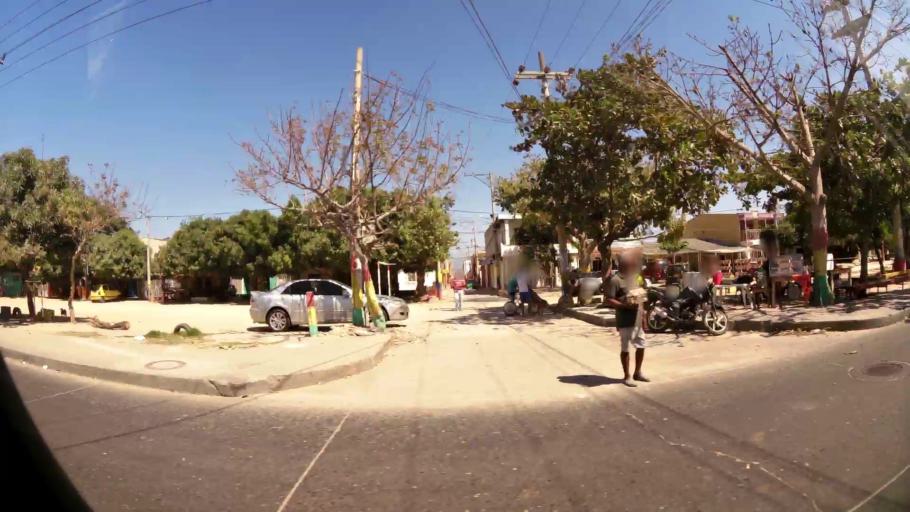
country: CO
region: Atlantico
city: Barranquilla
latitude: 10.9554
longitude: -74.7741
